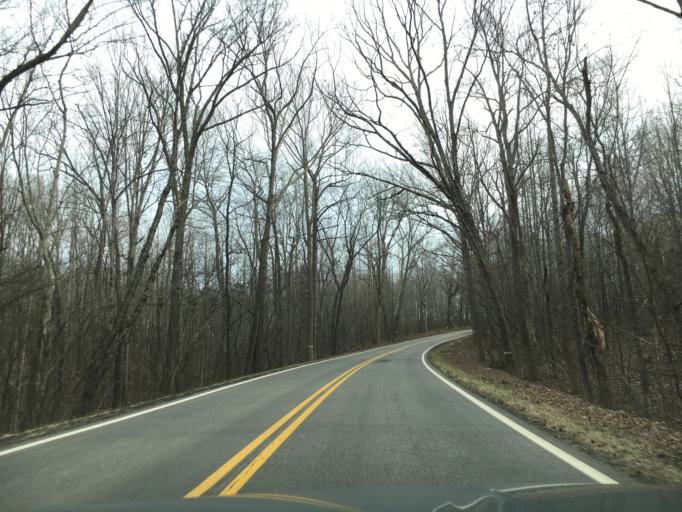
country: US
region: Virginia
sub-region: Charlotte County
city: Charlotte Court House
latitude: 37.1132
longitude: -78.7505
